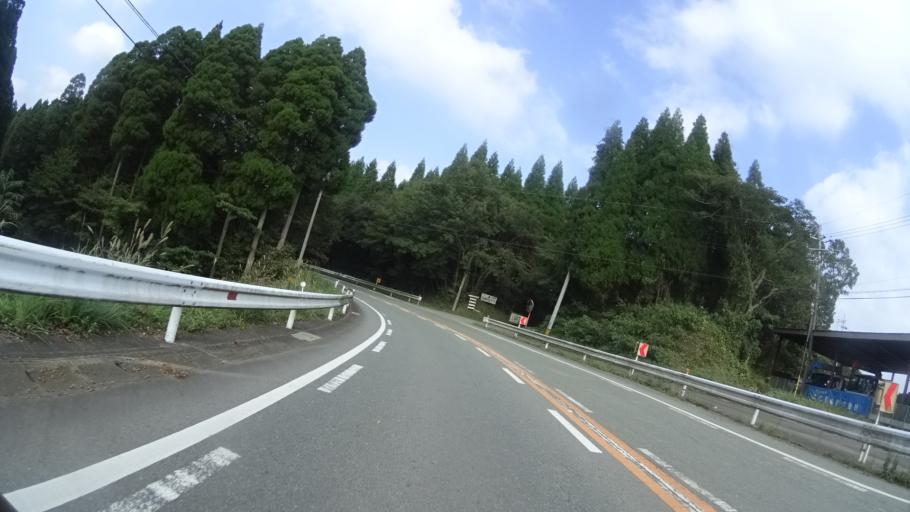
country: JP
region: Kumamoto
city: Aso
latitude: 33.0615
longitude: 131.0671
